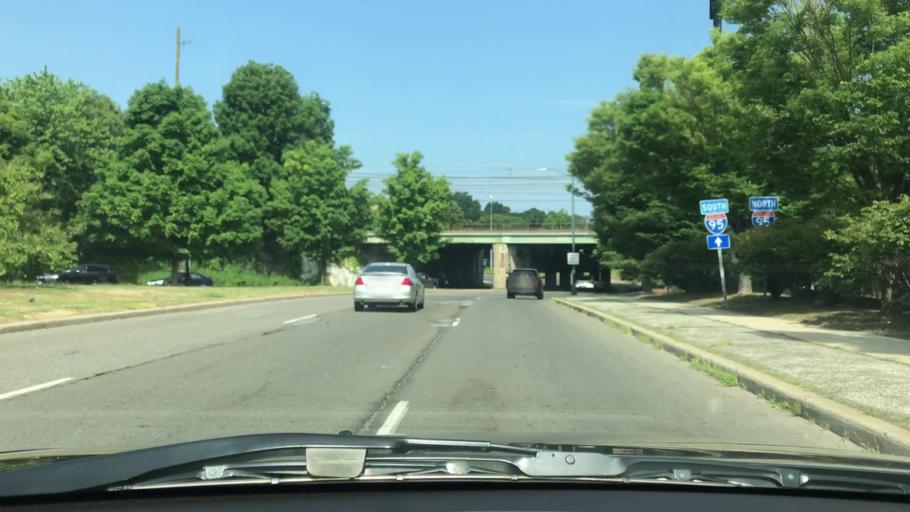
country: US
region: New York
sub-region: Westchester County
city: New Rochelle
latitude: 40.9157
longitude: -73.7793
